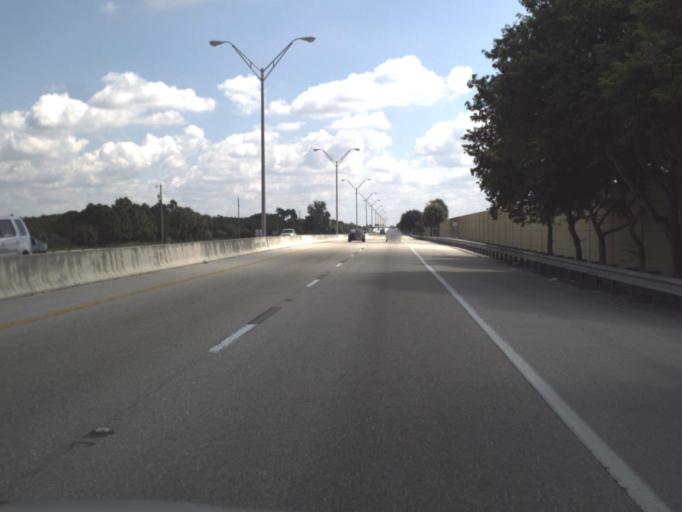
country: US
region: Florida
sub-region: Lee County
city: Lochmoor Waterway Estates
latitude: 26.6077
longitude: -81.9239
